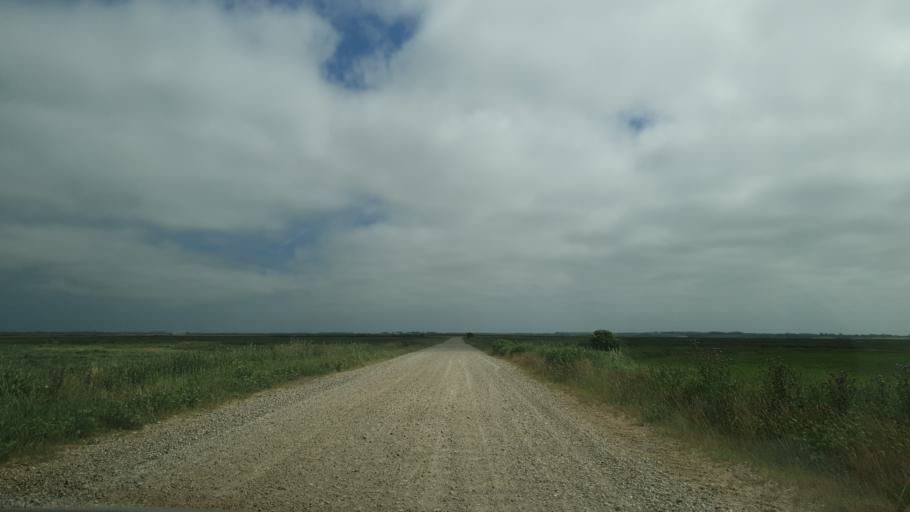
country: DK
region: Central Jutland
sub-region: Ringkobing-Skjern Kommune
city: Skjern
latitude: 55.9335
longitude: 8.4400
